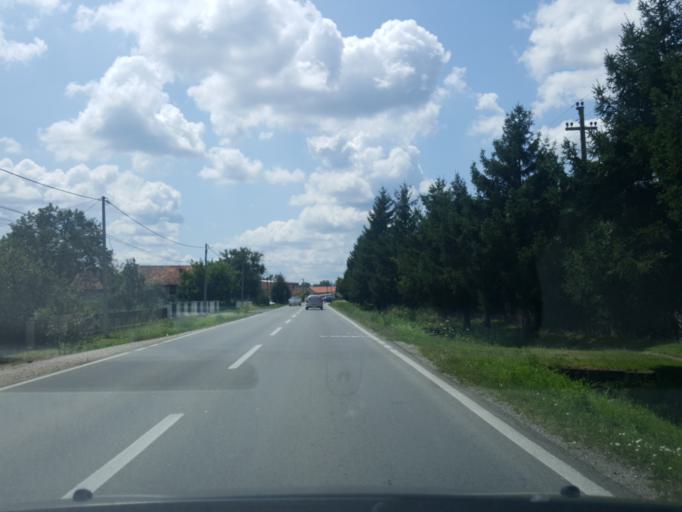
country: RS
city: Ribari
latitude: 44.7157
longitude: 19.4396
